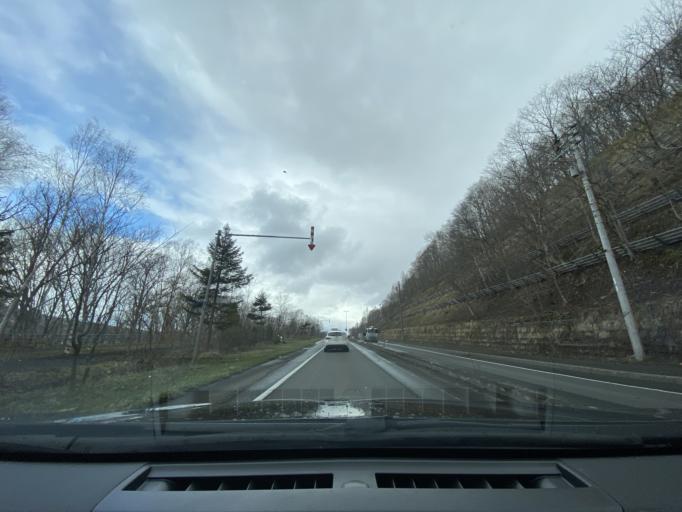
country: JP
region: Hokkaido
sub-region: Asahikawa-shi
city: Asahikawa
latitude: 43.7589
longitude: 142.2770
